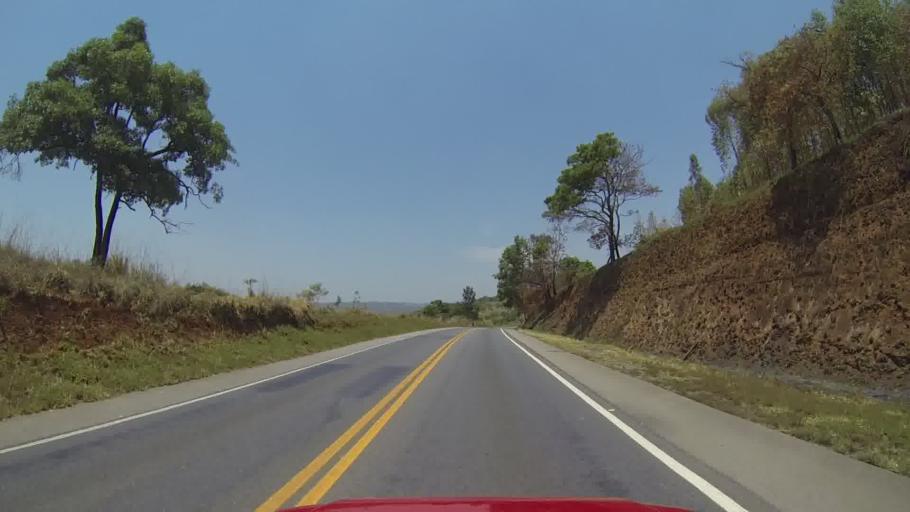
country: BR
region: Minas Gerais
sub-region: Itapecerica
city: Itapecerica
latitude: -20.3150
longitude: -45.2213
